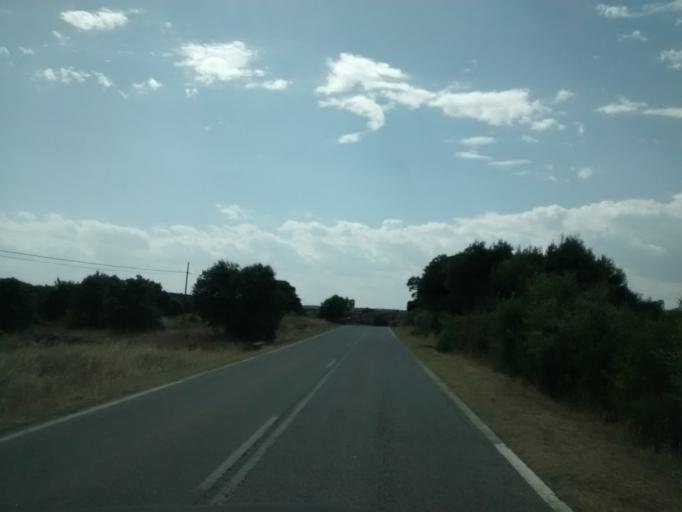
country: ES
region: Castille and Leon
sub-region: Provincia de Segovia
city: Pedraza
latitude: 41.1299
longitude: -3.8011
